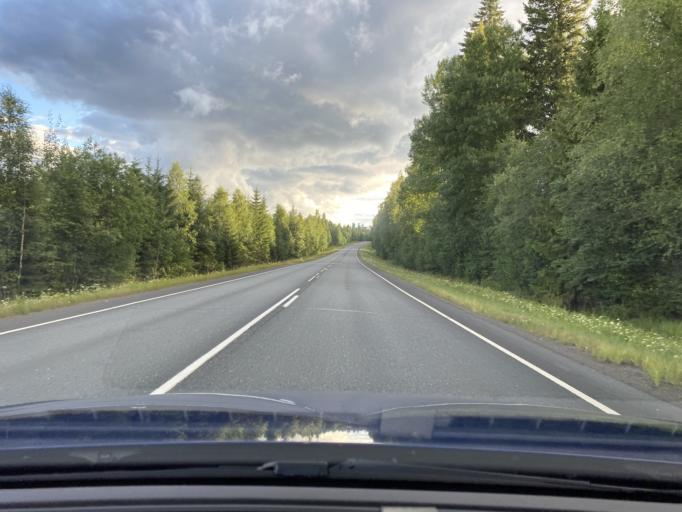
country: FI
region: Haeme
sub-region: Haemeenlinna
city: Renko
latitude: 60.8516
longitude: 24.1544
